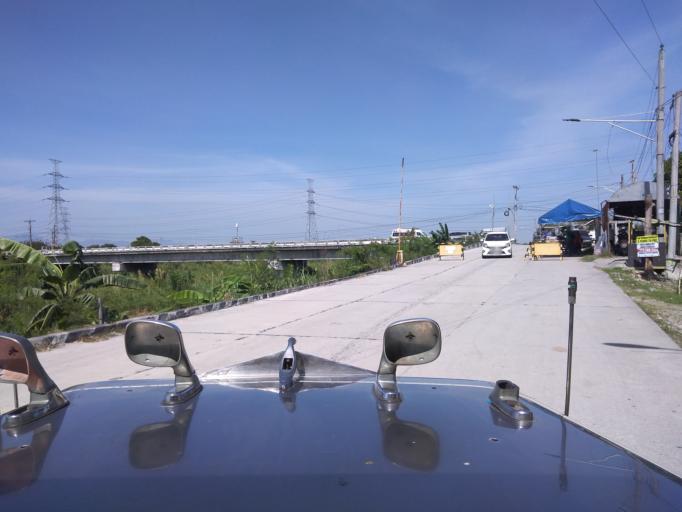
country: PH
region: Central Luzon
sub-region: Province of Pampanga
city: Bacolor
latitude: 15.0069
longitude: 120.6589
